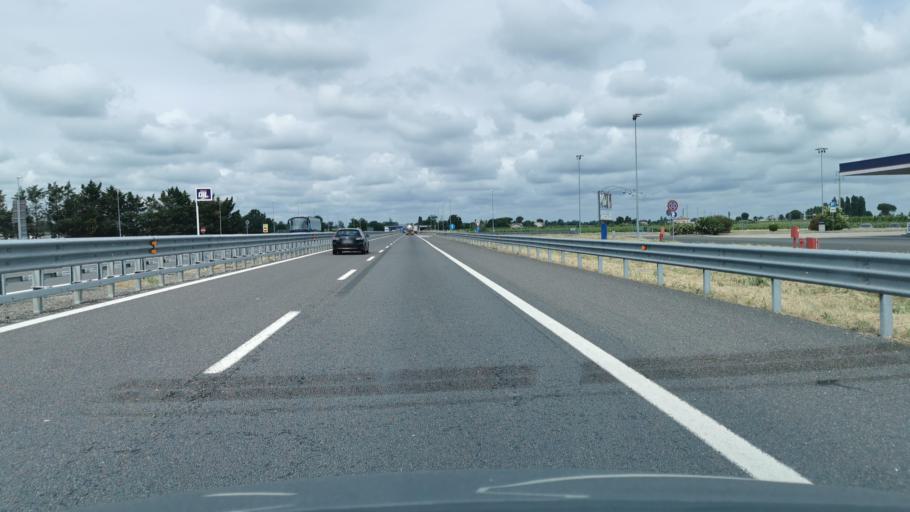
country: IT
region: Emilia-Romagna
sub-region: Provincia di Ravenna
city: Russi
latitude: 44.4026
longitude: 12.0459
